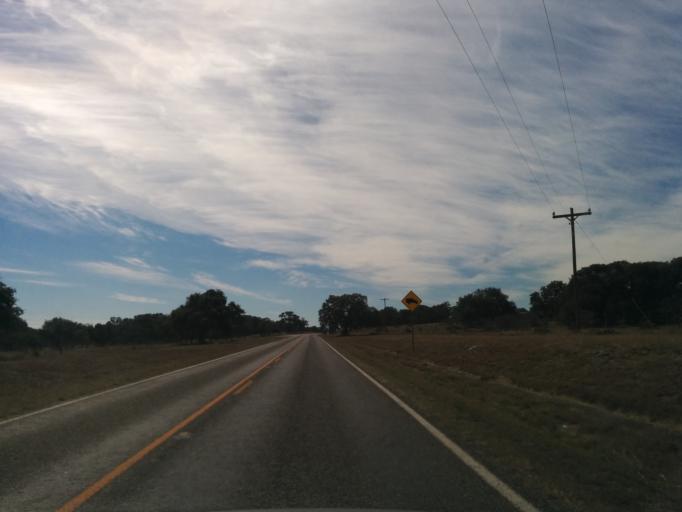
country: US
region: Texas
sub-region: Blanco County
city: Blanco
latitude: 29.9428
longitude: -98.5656
